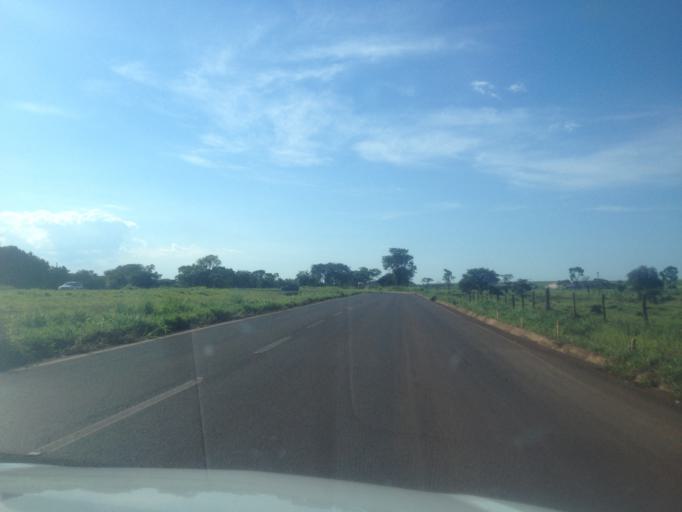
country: BR
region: Goias
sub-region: Cacu
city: Cacu
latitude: -18.3058
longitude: -51.1451
